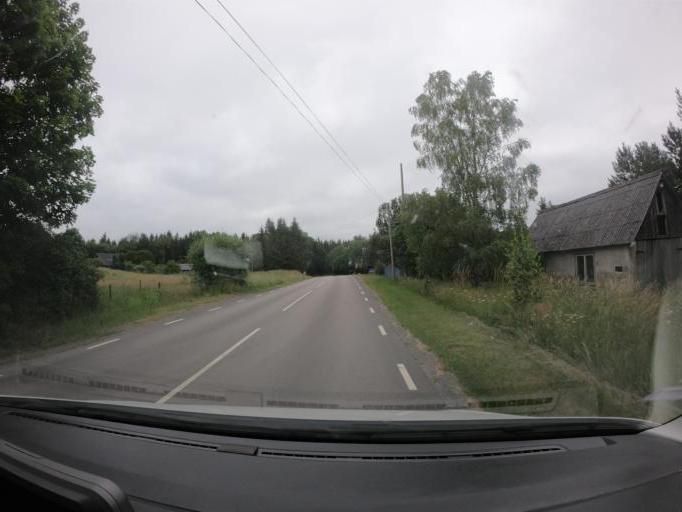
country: SE
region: Skane
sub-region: Perstorps Kommun
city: Perstorp
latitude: 56.0876
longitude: 13.3989
